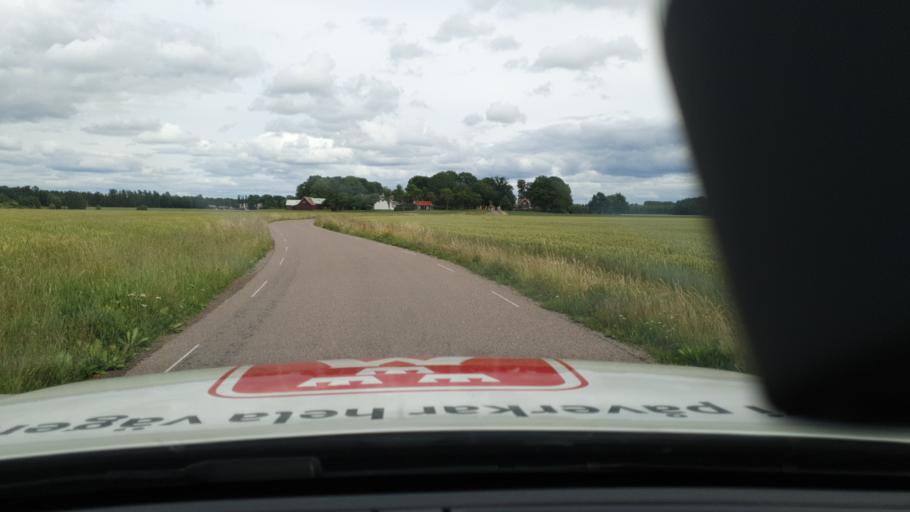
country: SE
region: Vaestra Goetaland
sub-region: Lidkopings Kommun
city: Vinninga
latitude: 58.3895
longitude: 13.2968
